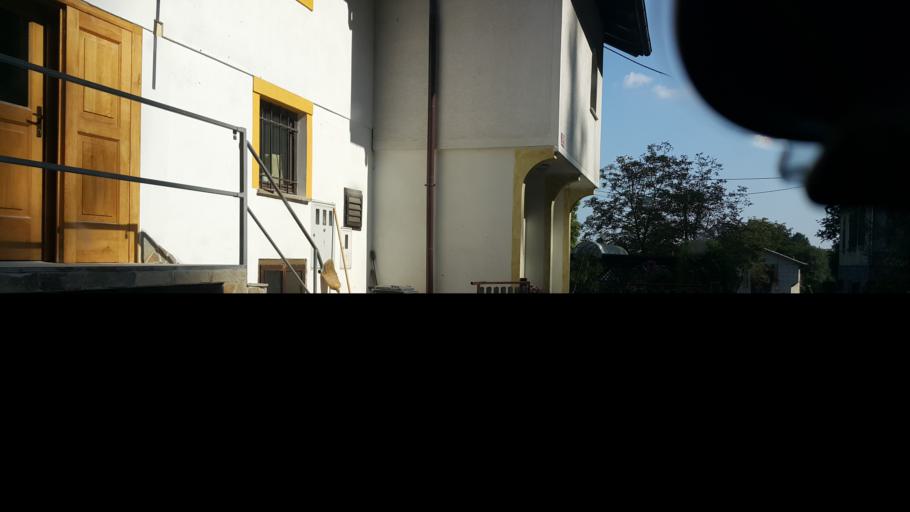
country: SI
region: Race-Fram
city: Fram
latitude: 46.4531
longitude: 15.6344
